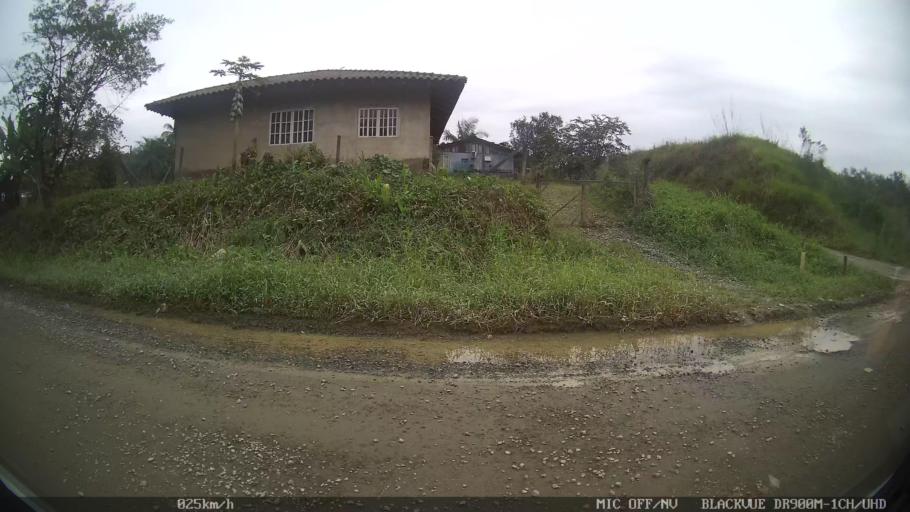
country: BR
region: Santa Catarina
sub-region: Joinville
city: Joinville
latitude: -26.2774
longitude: -48.8905
